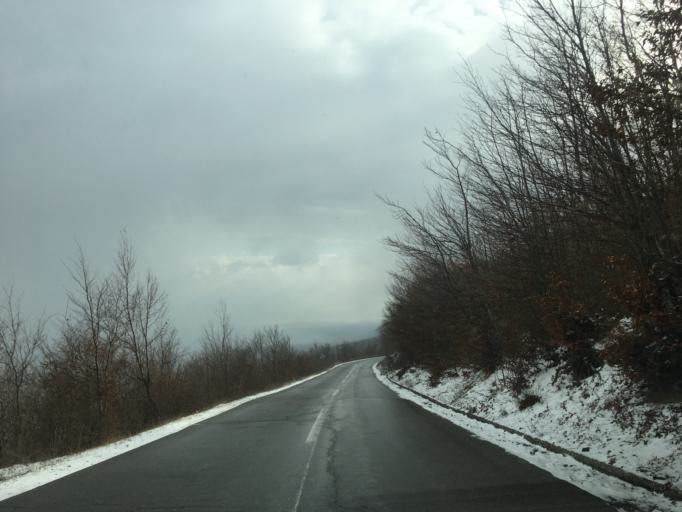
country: XK
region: Pec
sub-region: Komuna e Pejes
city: Dubova (Driloni)
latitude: 42.7575
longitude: 20.3010
